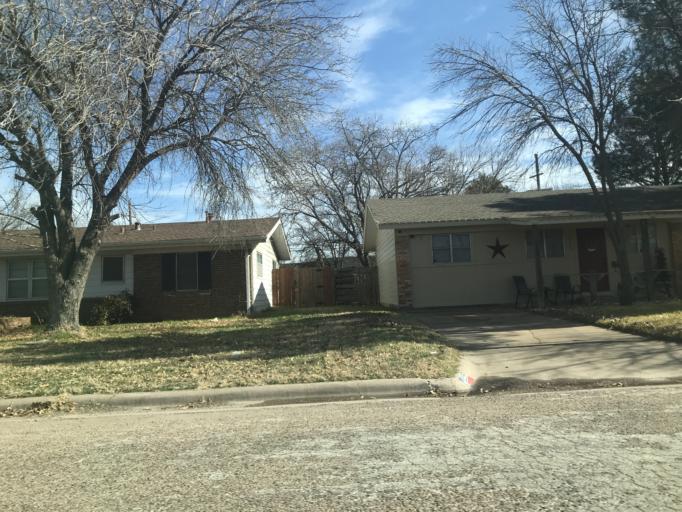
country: US
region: Texas
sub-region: Taylor County
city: Abilene
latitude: 32.4185
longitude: -99.7585
